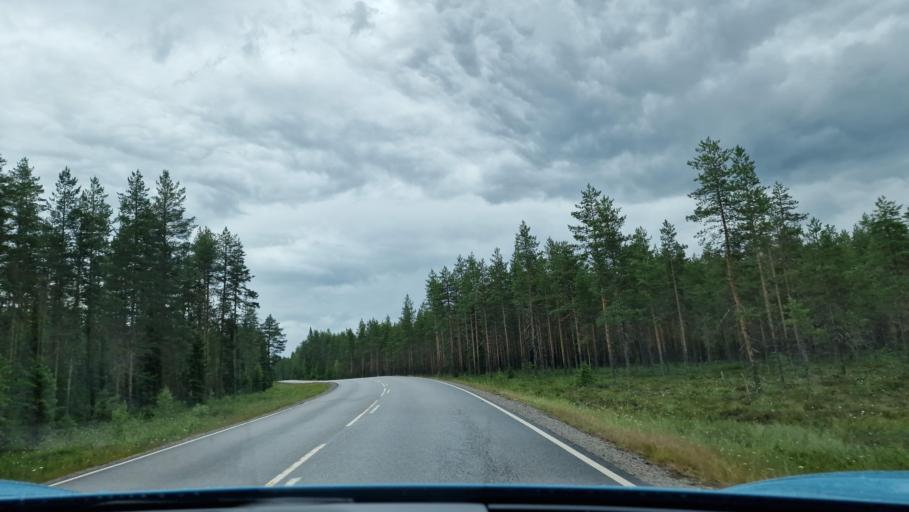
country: FI
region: Central Finland
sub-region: Saarijaervi-Viitasaari
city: Pylkoenmaeki
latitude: 62.6199
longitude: 24.5812
